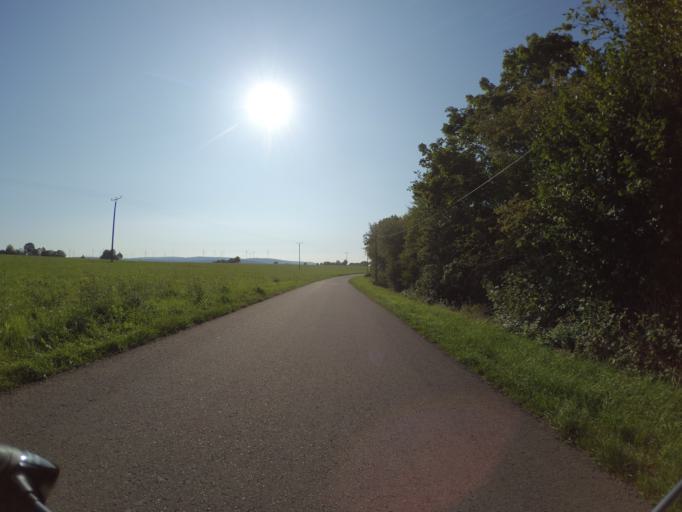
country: DE
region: Rheinland-Pfalz
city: Trittenheim
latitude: 49.8456
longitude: 6.9045
